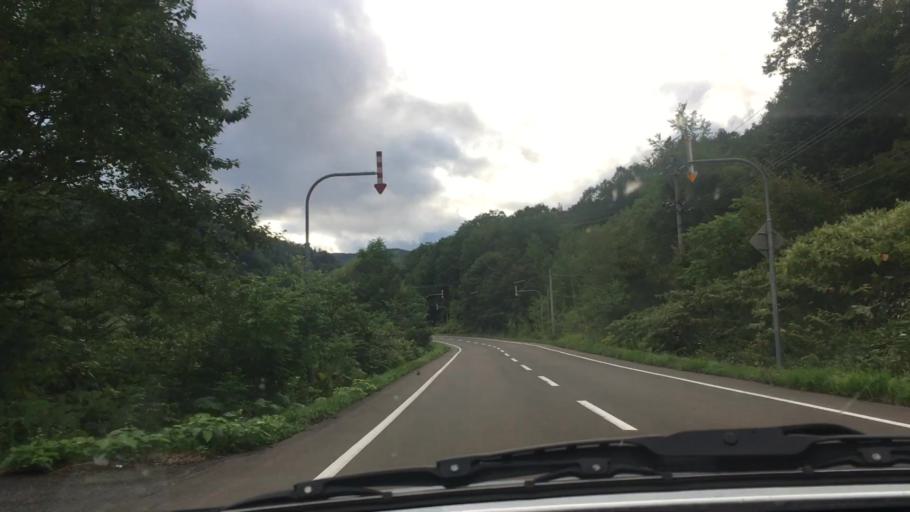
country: JP
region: Hokkaido
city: Shimo-furano
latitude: 43.0493
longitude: 142.5094
